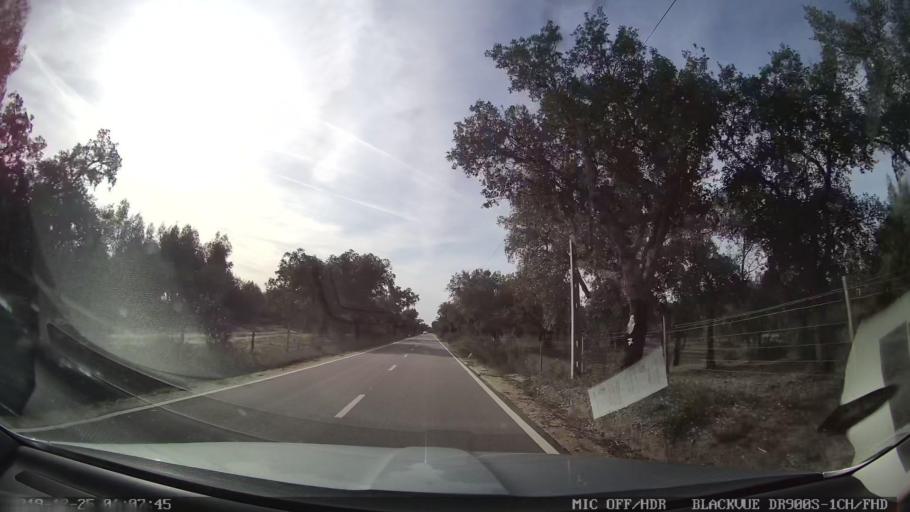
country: PT
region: Portalegre
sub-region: Nisa
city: Nisa
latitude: 39.4586
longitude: -7.7053
